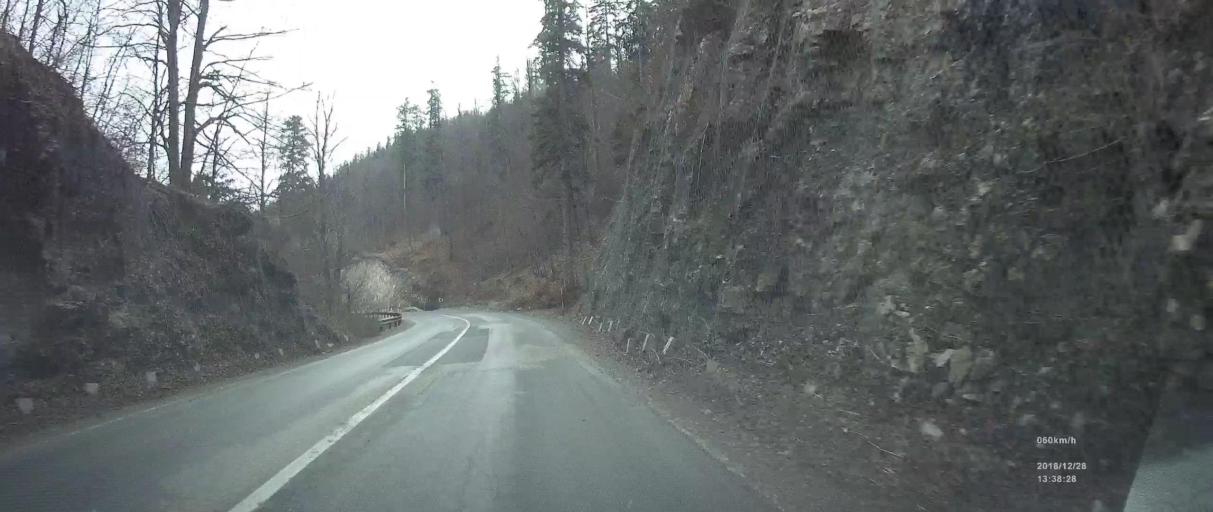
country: HR
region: Primorsko-Goranska
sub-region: Grad Delnice
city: Delnice
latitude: 45.3555
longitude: 14.7251
